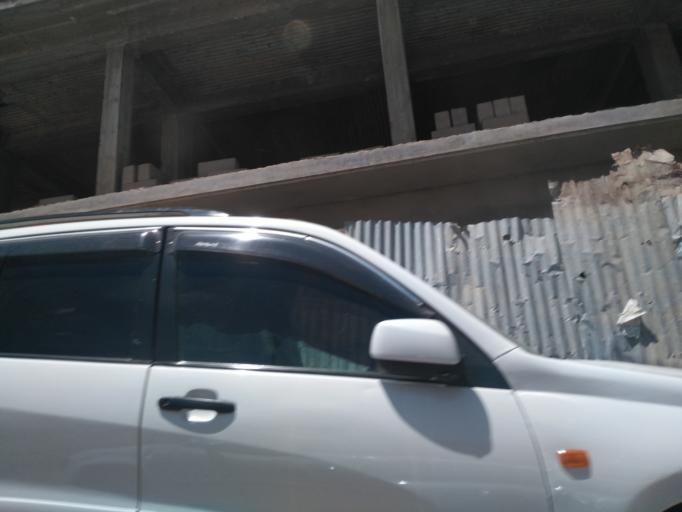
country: TZ
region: Mwanza
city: Mwanza
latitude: -2.5237
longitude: 32.9013
